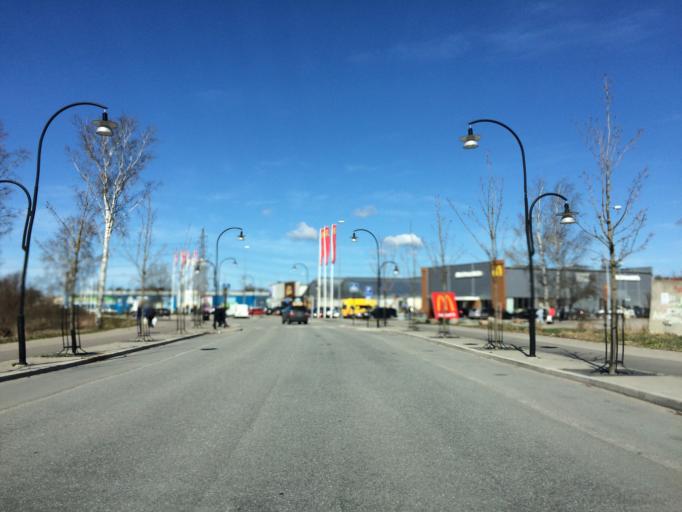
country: SE
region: Stockholm
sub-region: Sollentuna Kommun
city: Sollentuna
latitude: 59.4380
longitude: 17.9349
